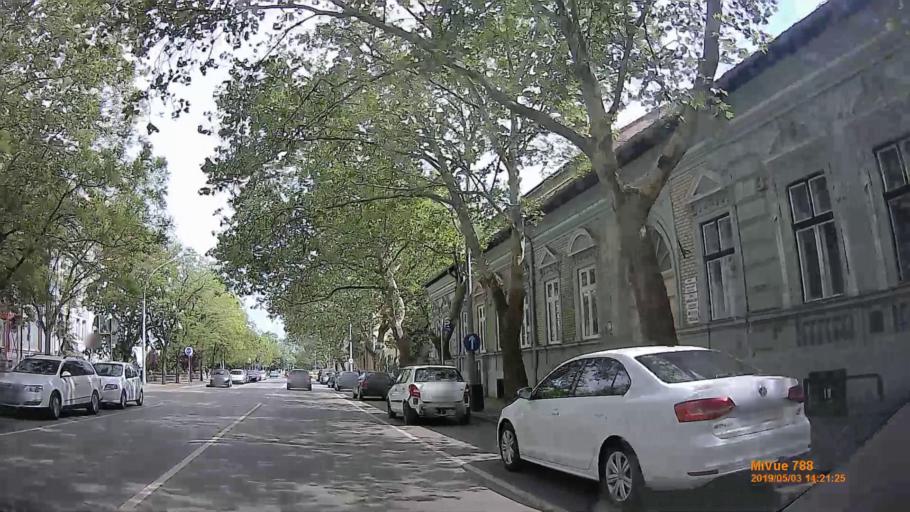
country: HU
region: Jasz-Nagykun-Szolnok
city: Szolnok
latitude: 47.1775
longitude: 20.1823
